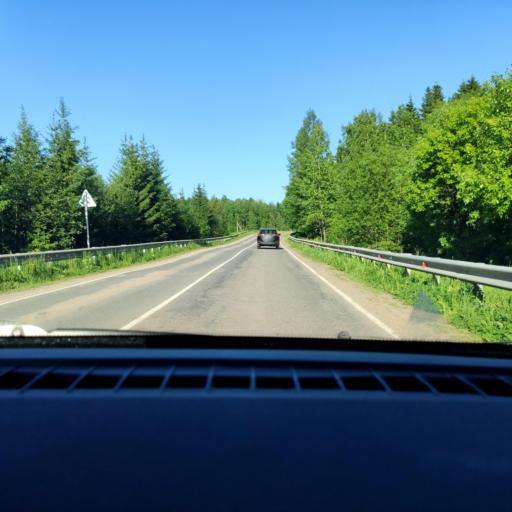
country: RU
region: Perm
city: Overyata
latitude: 58.1255
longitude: 55.8573
